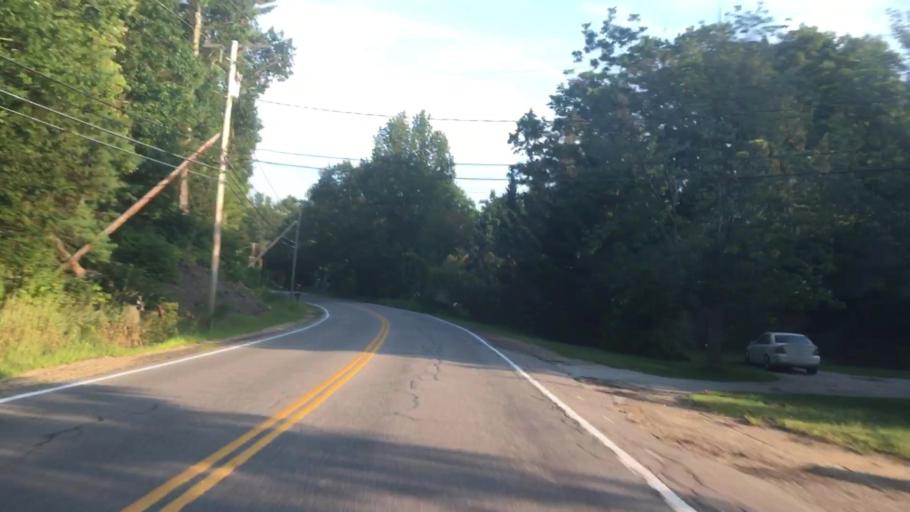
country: US
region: New Hampshire
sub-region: Belknap County
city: Gilmanton
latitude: 43.4718
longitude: -71.4280
